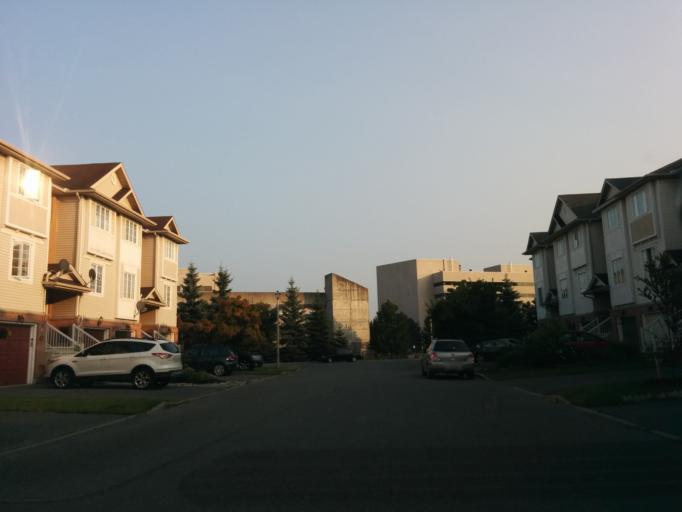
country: CA
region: Ontario
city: Ottawa
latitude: 45.3664
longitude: -75.7342
